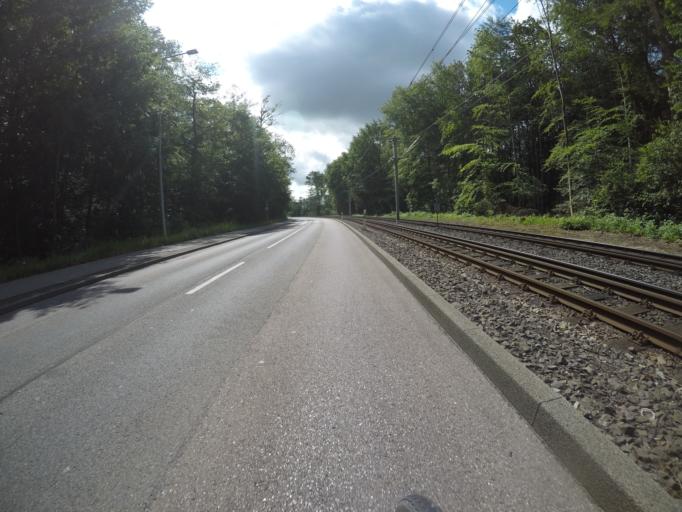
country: DE
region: Baden-Wuerttemberg
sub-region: Regierungsbezirk Stuttgart
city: Stuttgart-Ost
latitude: 48.7497
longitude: 9.2026
